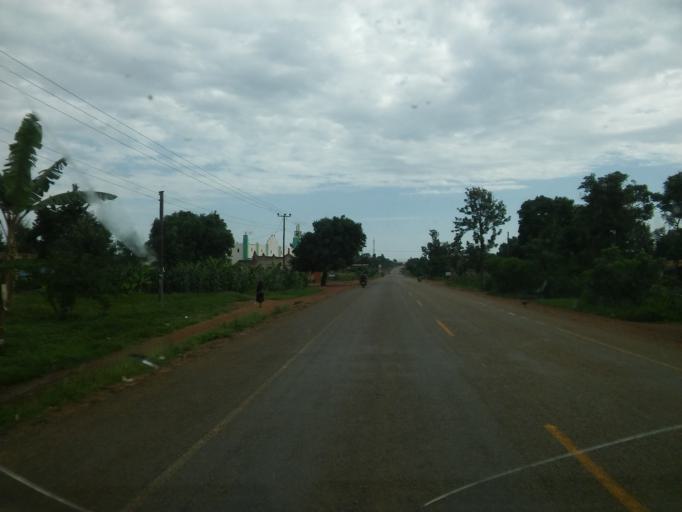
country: UG
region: Eastern Region
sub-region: Mbale District
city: Mbale
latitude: 1.1326
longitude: 34.1664
